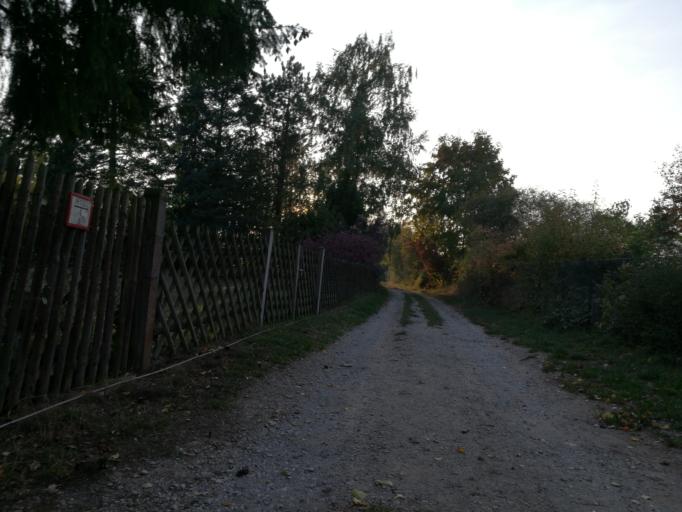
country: DE
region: Bavaria
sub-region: Regierungsbezirk Mittelfranken
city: Seukendorf
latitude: 49.4838
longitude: 10.9244
